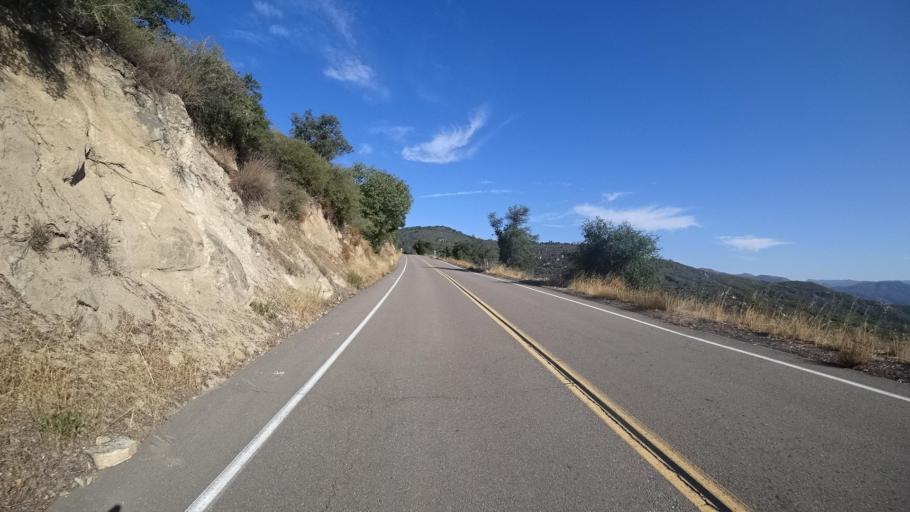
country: US
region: California
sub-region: Riverside County
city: Aguanga
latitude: 33.2641
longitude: -116.7665
